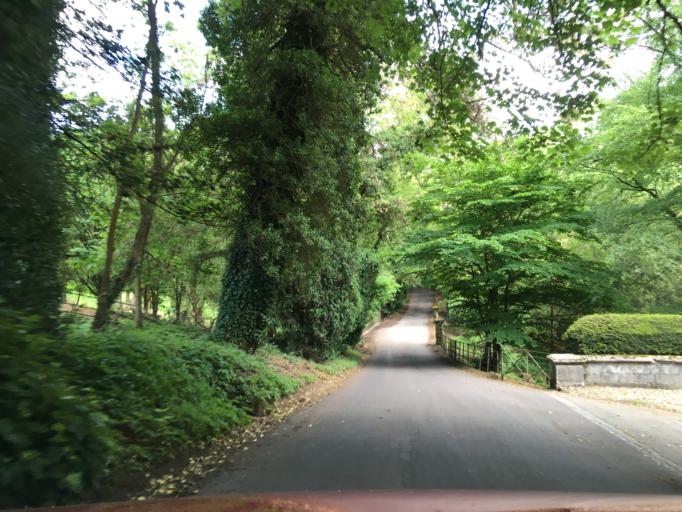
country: GB
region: England
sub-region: Gloucestershire
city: Charlton Kings
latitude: 51.8321
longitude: -2.0514
